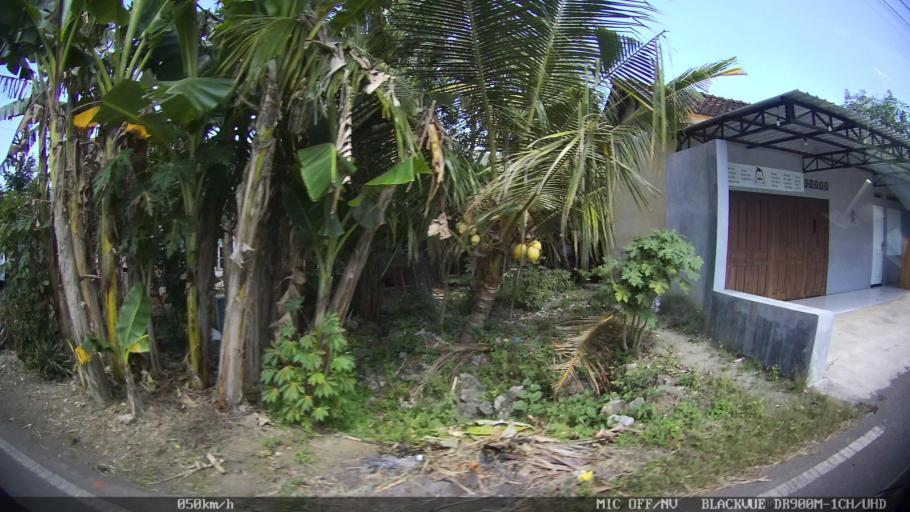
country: ID
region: Daerah Istimewa Yogyakarta
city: Pundong
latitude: -7.9809
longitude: 110.3372
